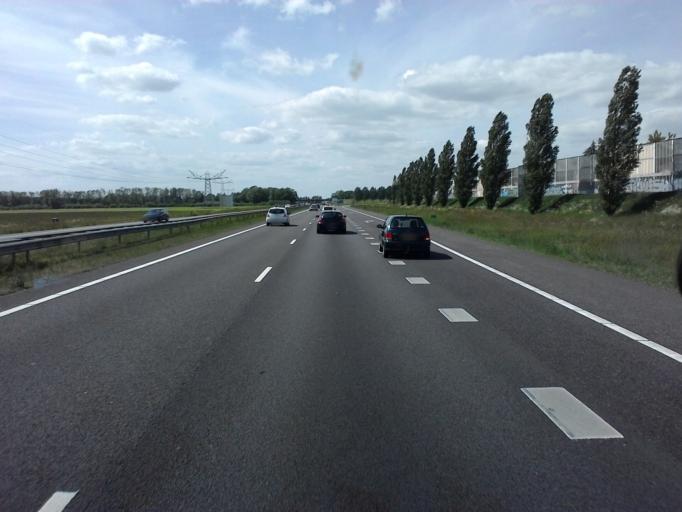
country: NL
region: Gelderland
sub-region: Gemeente Beuningen
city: Beuningen
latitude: 51.8486
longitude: 5.7574
